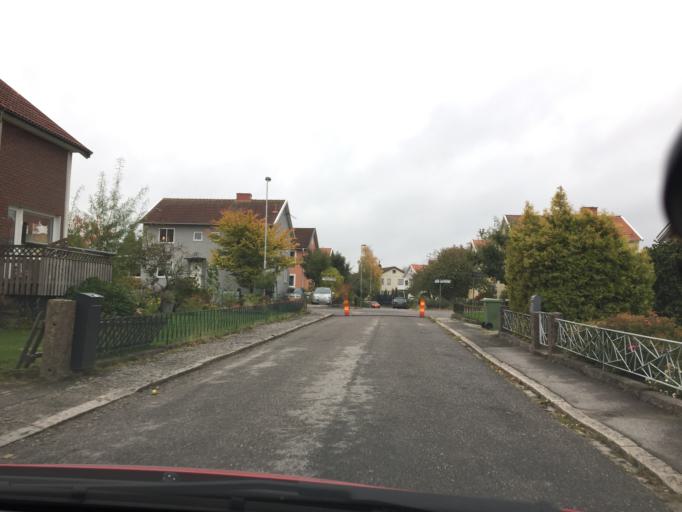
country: SE
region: Vaestra Goetaland
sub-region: Trollhattan
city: Trollhattan
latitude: 58.2904
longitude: 12.3200
